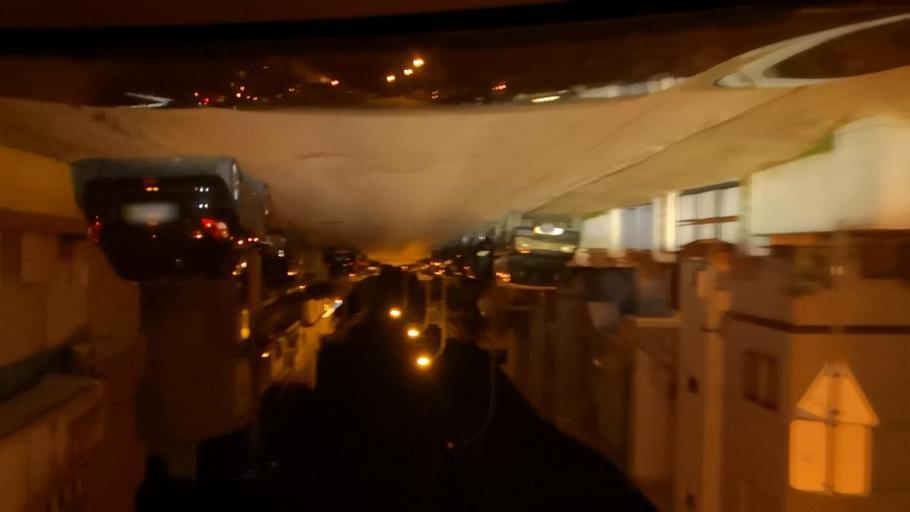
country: PT
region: Setubal
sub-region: Setubal
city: Setubal
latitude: 38.5296
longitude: -8.9051
